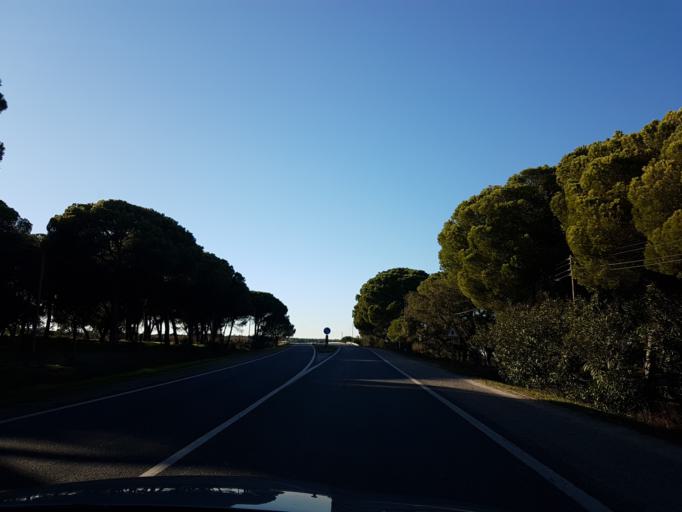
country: PT
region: Setubal
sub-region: Alcacer do Sal
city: Alcacer do Sal
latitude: 38.3610
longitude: -8.5183
